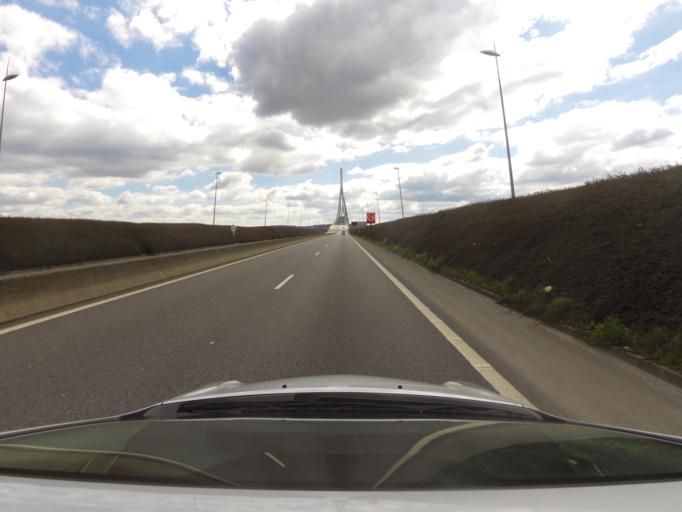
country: FR
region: Lower Normandy
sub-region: Departement du Calvados
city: La Riviere-Saint-Sauveur
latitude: 49.4461
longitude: 0.2720
